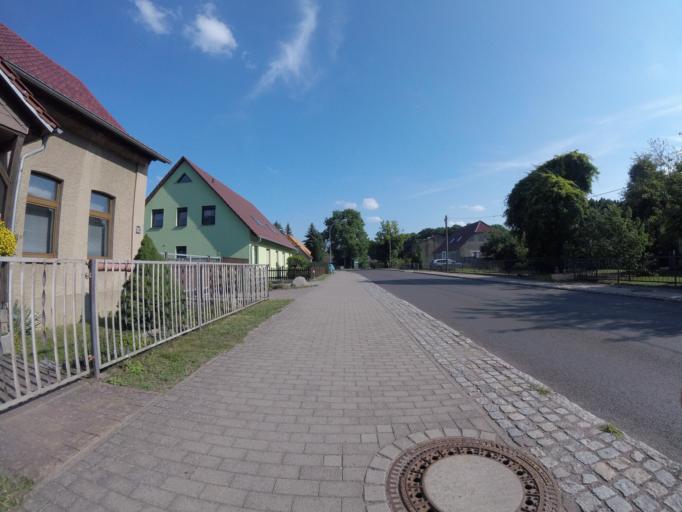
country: DE
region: Brandenburg
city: Bliesdorf
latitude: 52.6906
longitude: 14.1411
